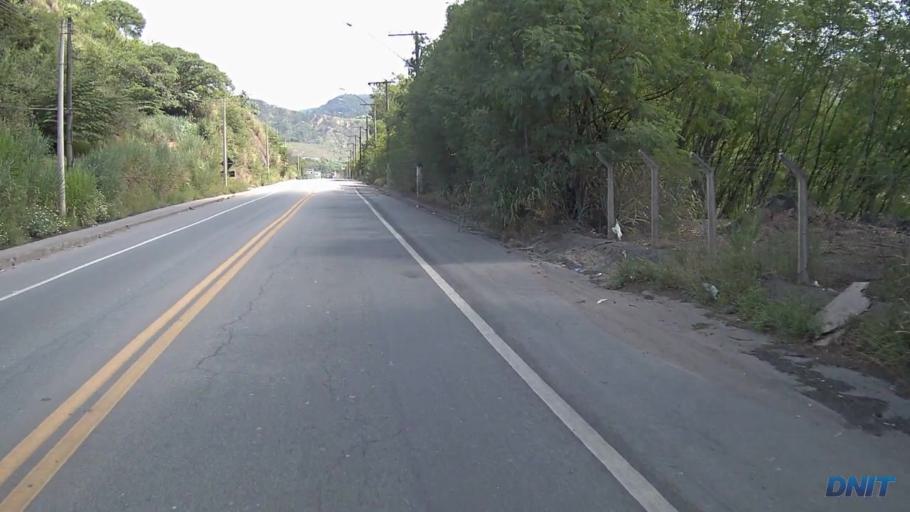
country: BR
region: Minas Gerais
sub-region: Coronel Fabriciano
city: Coronel Fabriciano
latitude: -19.5288
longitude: -42.6531
